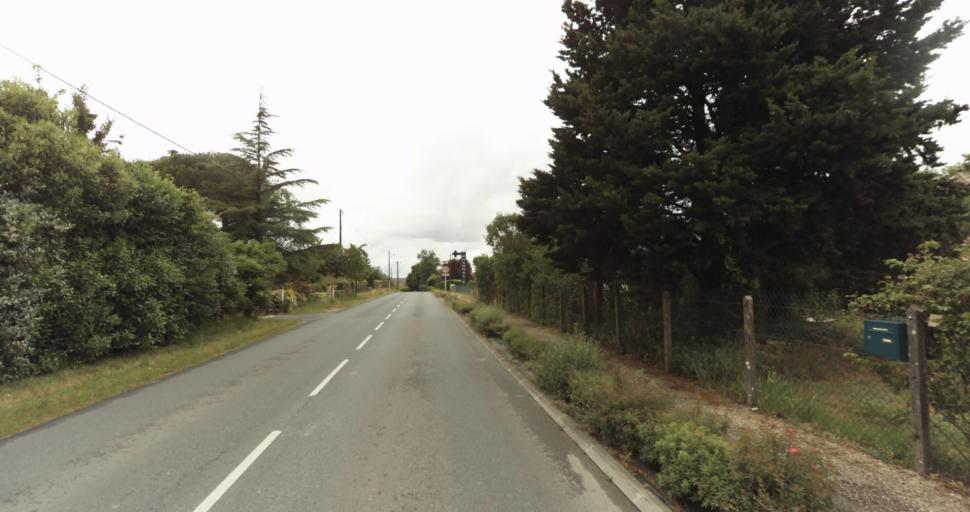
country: FR
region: Aquitaine
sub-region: Departement de la Dordogne
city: Beaumont-du-Perigord
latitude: 44.7608
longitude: 0.7712
